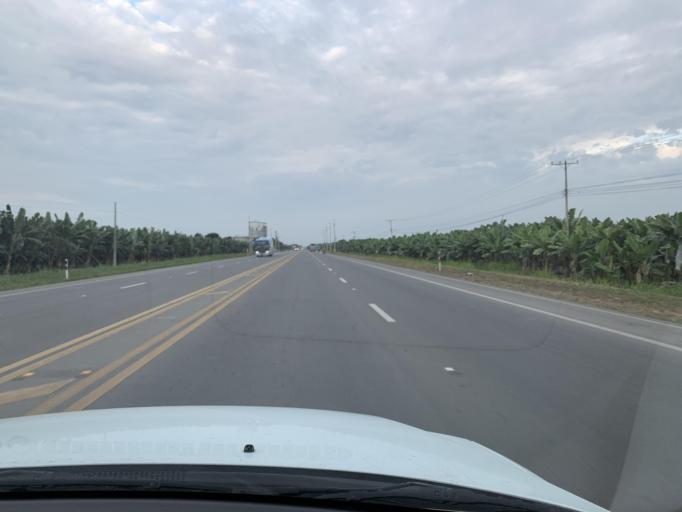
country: EC
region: Guayas
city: Yaguachi Nuevo
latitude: -2.2545
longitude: -79.6208
